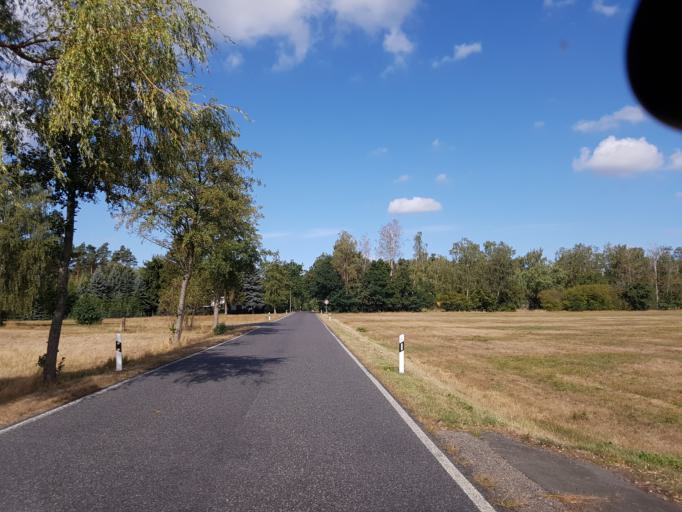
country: DE
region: Brandenburg
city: Sonnewalde
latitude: 51.7369
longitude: 13.6252
